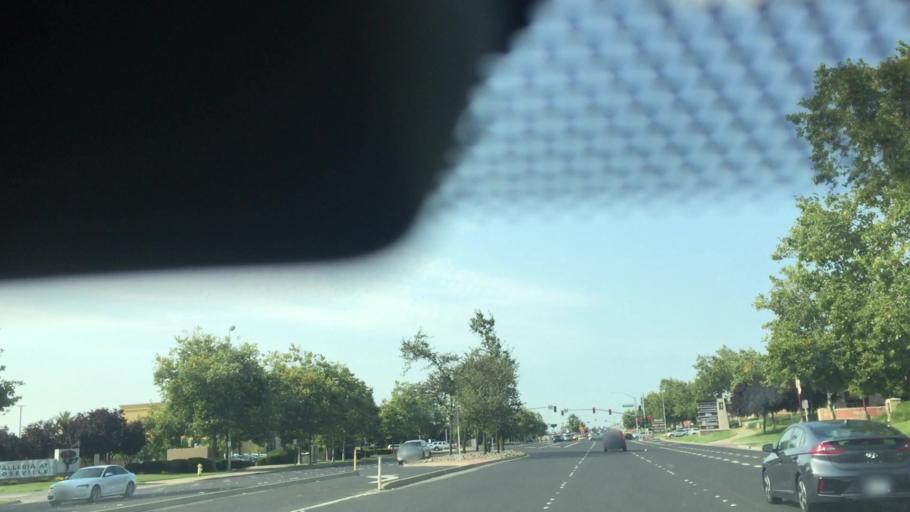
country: US
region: California
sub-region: Placer County
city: Roseville
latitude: 38.7702
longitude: -121.2657
